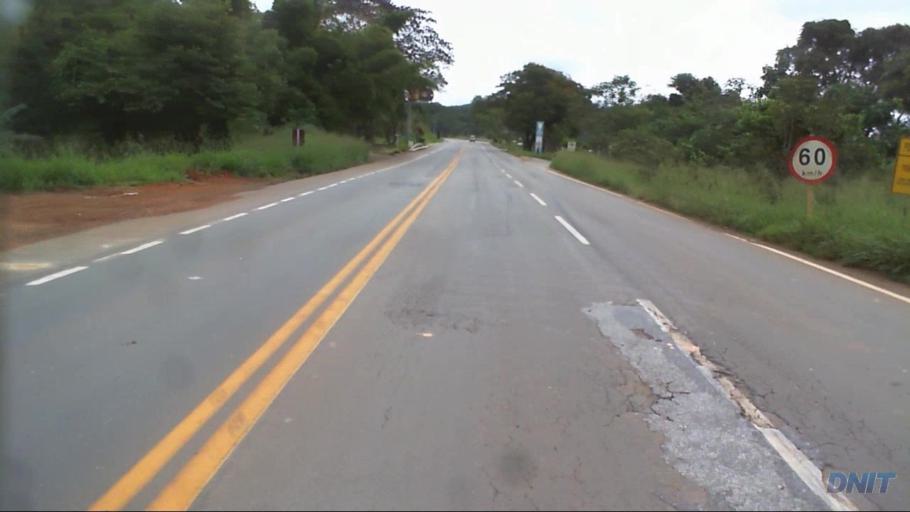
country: BR
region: Minas Gerais
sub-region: Barao De Cocais
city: Barao de Cocais
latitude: -19.8311
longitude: -43.3546
